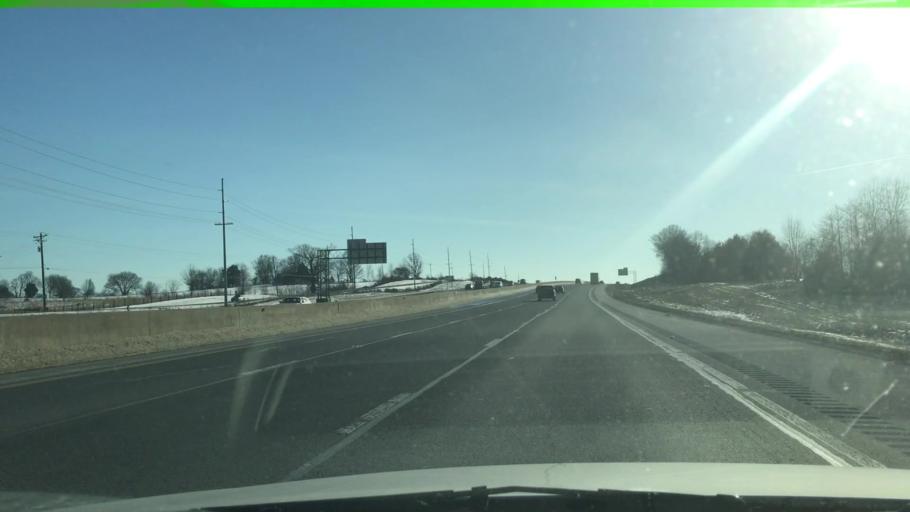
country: US
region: Kentucky
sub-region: Warren County
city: Bowling Green
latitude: 36.9679
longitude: -86.3964
